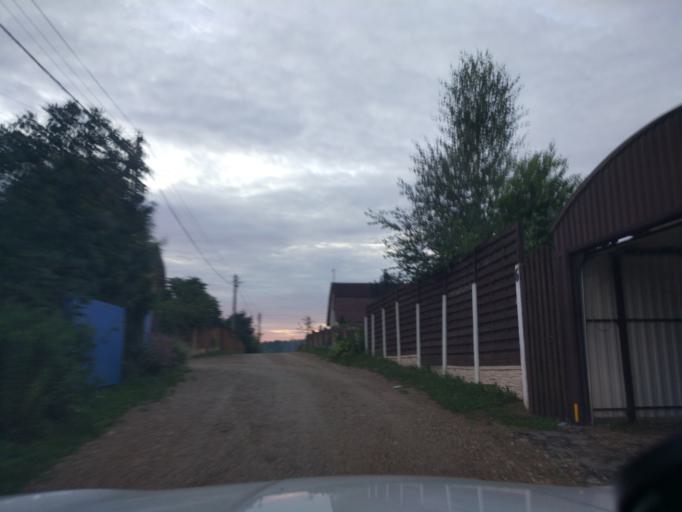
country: BY
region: Minsk
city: Astrashytski Haradok
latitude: 54.0886
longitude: 27.6982
